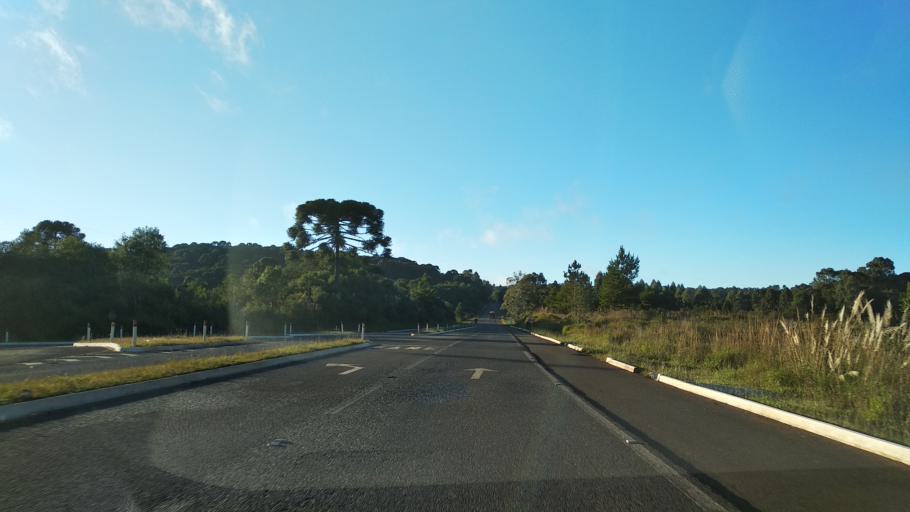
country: BR
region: Santa Catarina
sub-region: Correia Pinto
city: Correia Pinto
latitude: -27.6267
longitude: -50.6248
